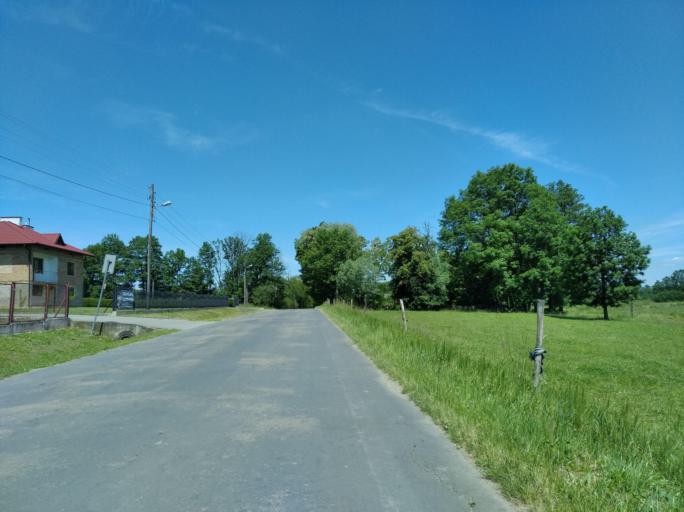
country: PL
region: Subcarpathian Voivodeship
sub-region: Powiat jasielski
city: Tarnowiec
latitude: 49.7027
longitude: 21.5527
